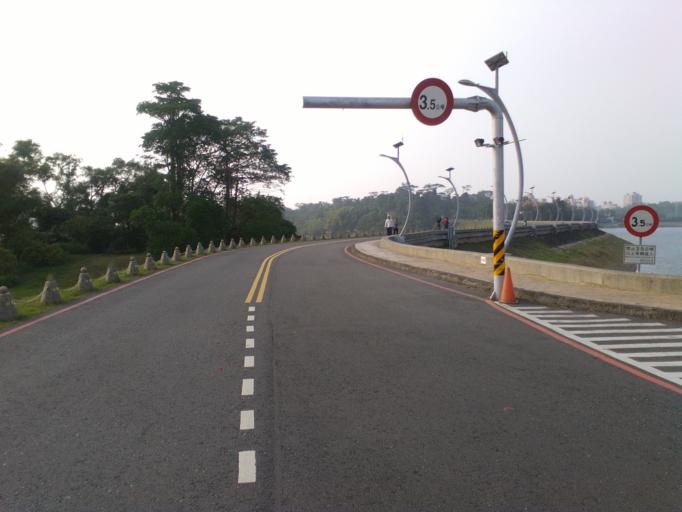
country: TW
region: Taiwan
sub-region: Chiayi
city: Jiayi Shi
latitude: 23.4653
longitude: 120.4800
